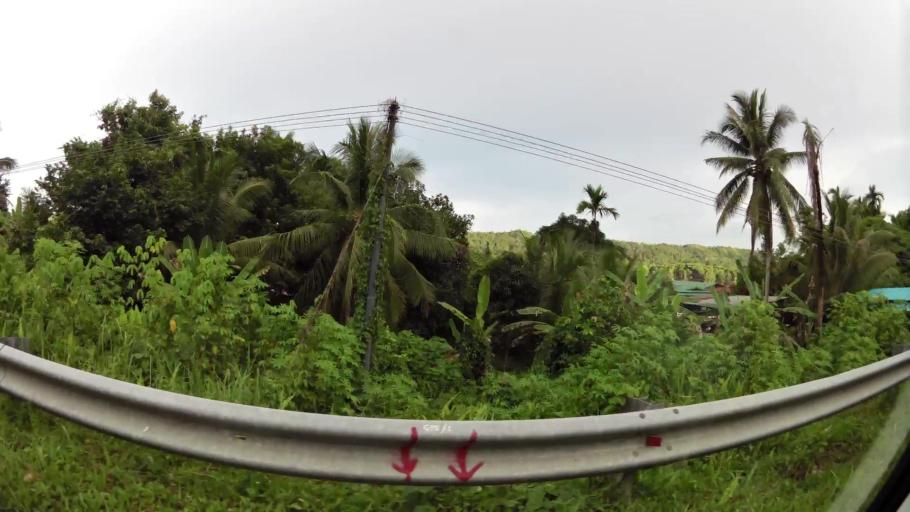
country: BN
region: Brunei and Muara
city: Bandar Seri Begawan
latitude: 4.8997
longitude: 114.9876
